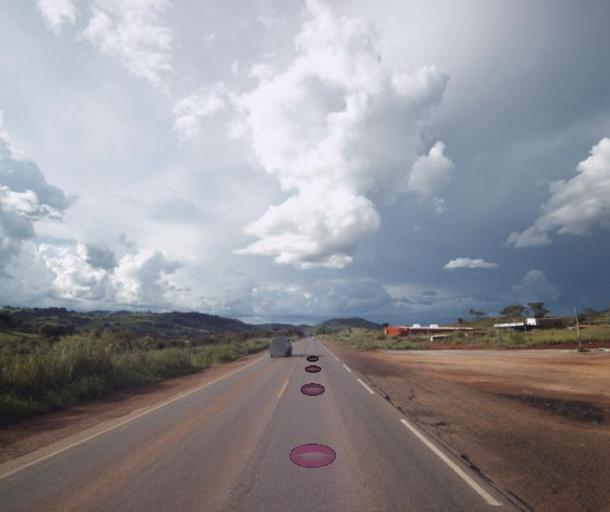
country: BR
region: Goias
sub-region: Rialma
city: Rialma
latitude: -15.3045
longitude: -49.5709
